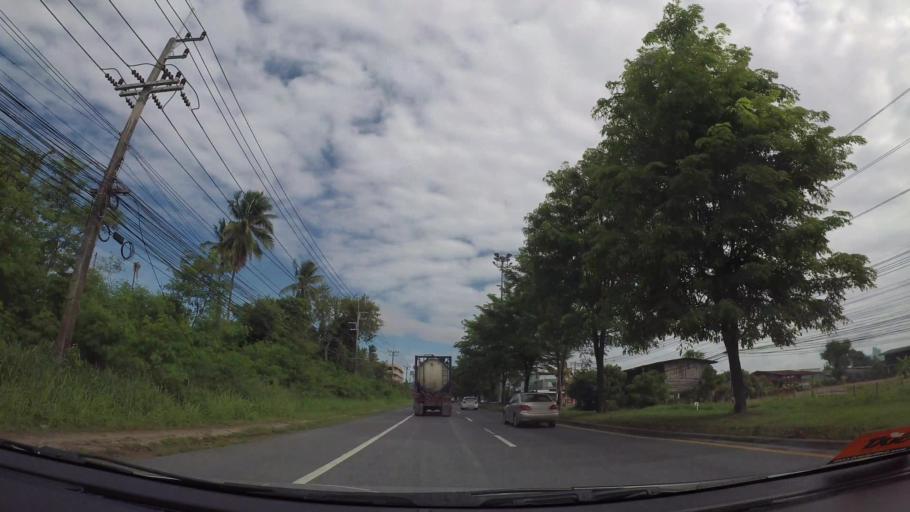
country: TH
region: Rayong
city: Ban Chang
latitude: 12.7368
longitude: 101.1281
